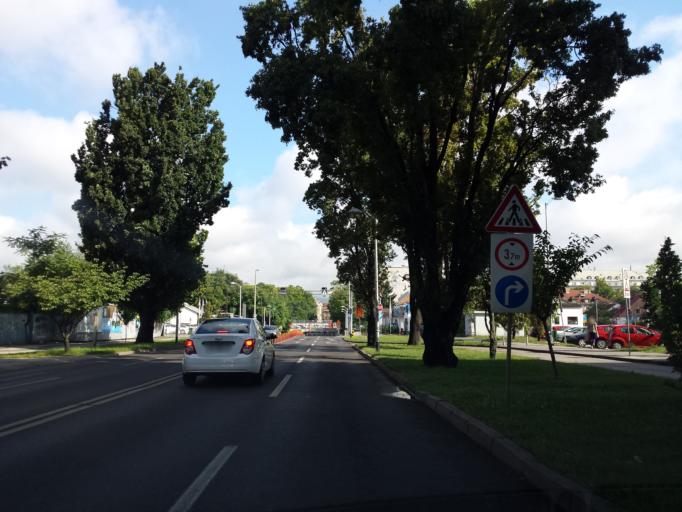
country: HR
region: Grad Zagreb
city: Zagreb - Centar
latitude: 45.8022
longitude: 15.9744
